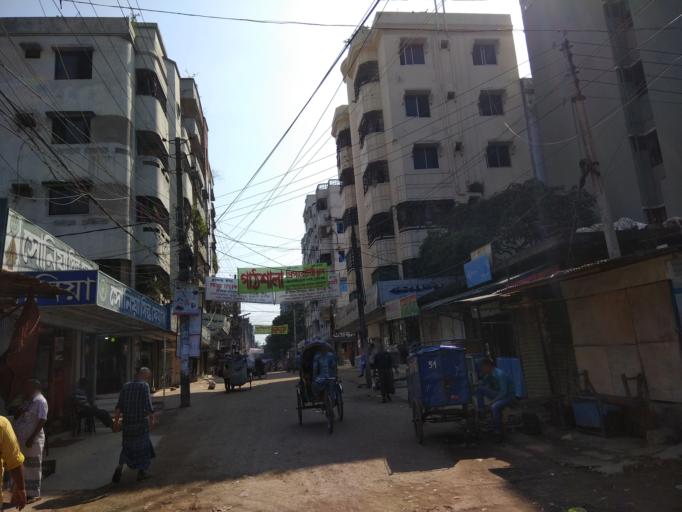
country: BD
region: Dhaka
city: Tungi
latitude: 23.8172
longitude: 90.3708
